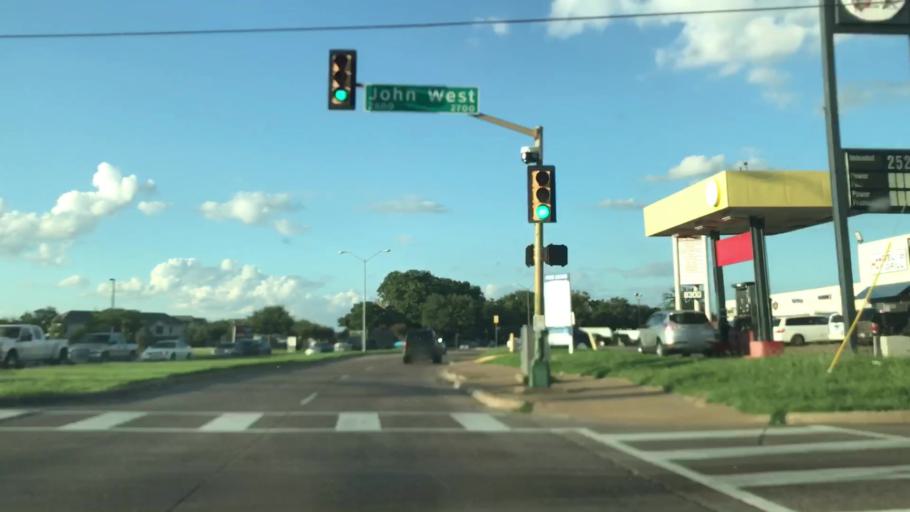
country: US
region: Texas
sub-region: Dallas County
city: Mesquite
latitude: 32.8071
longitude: -96.6681
